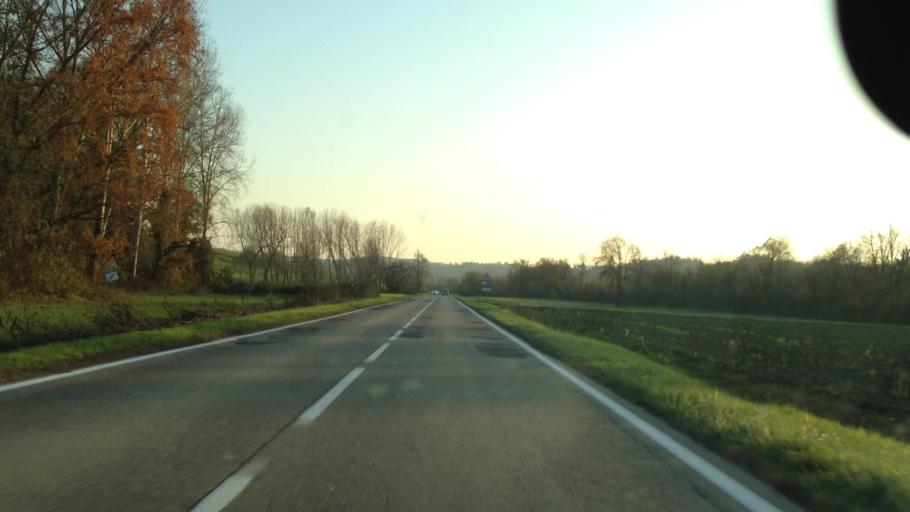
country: IT
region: Piedmont
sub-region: Provincia di Asti
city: Cunico
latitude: 45.0479
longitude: 8.1121
